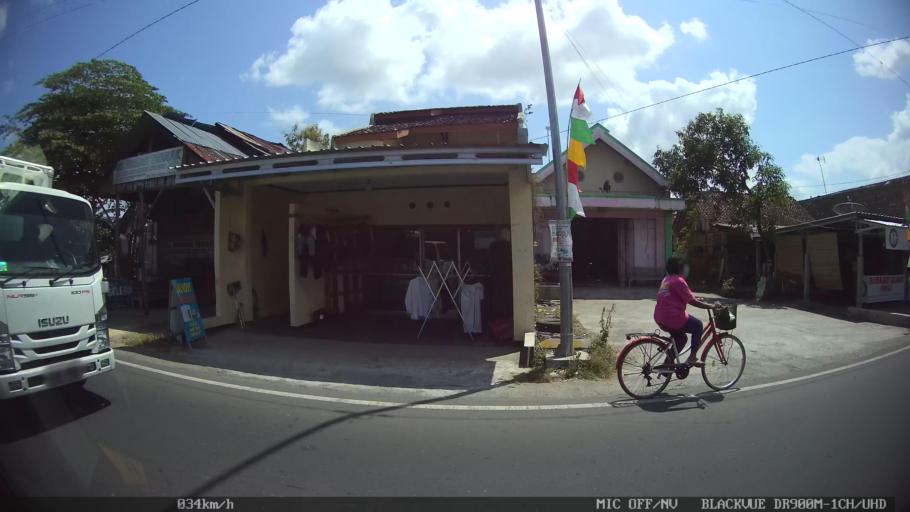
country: ID
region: Daerah Istimewa Yogyakarta
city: Sewon
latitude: -7.9137
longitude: 110.3824
